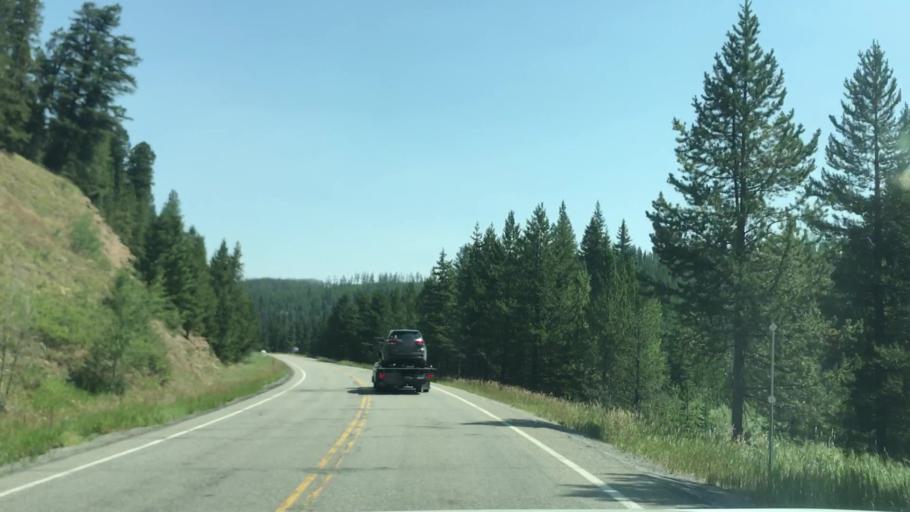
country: US
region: Montana
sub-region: Gallatin County
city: West Yellowstone
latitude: 44.8058
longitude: -111.1018
